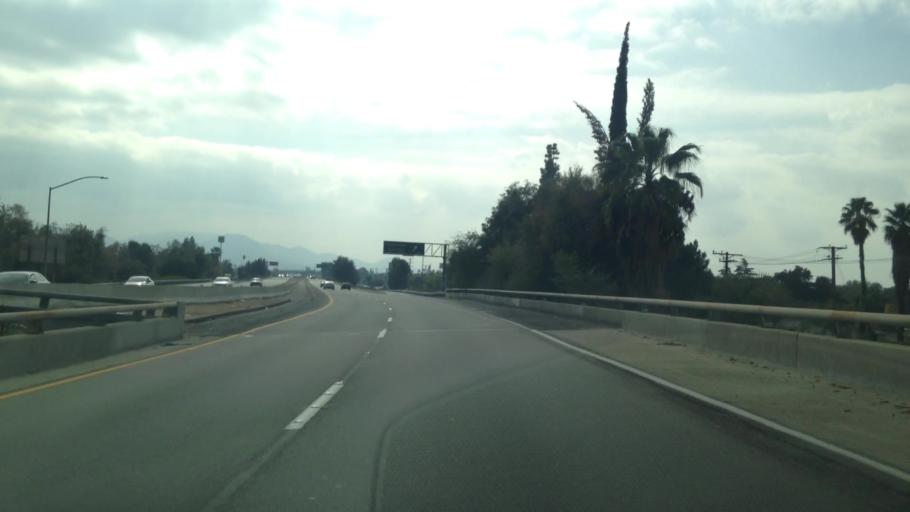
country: US
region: California
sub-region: San Bernardino County
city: San Bernardino
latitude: 34.1407
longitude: -117.3026
